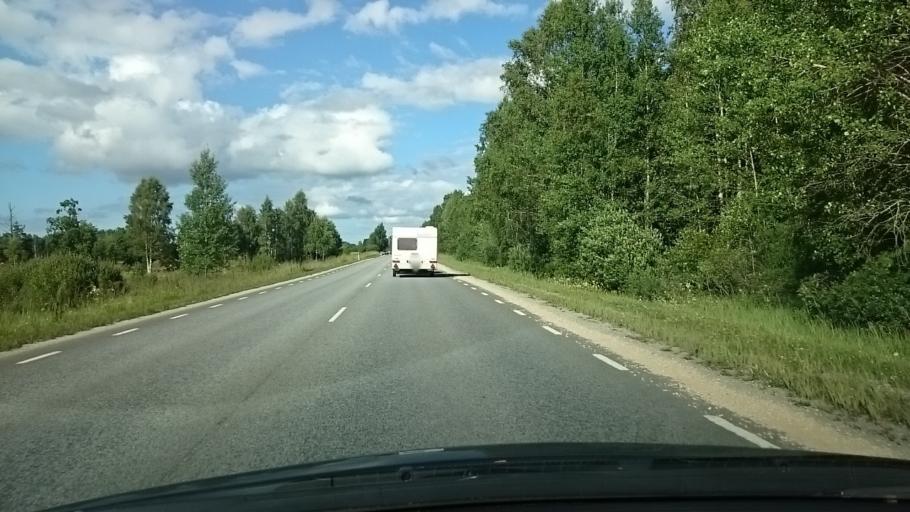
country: EE
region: Harju
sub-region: Keila linn
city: Keila
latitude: 59.2751
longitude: 24.2993
